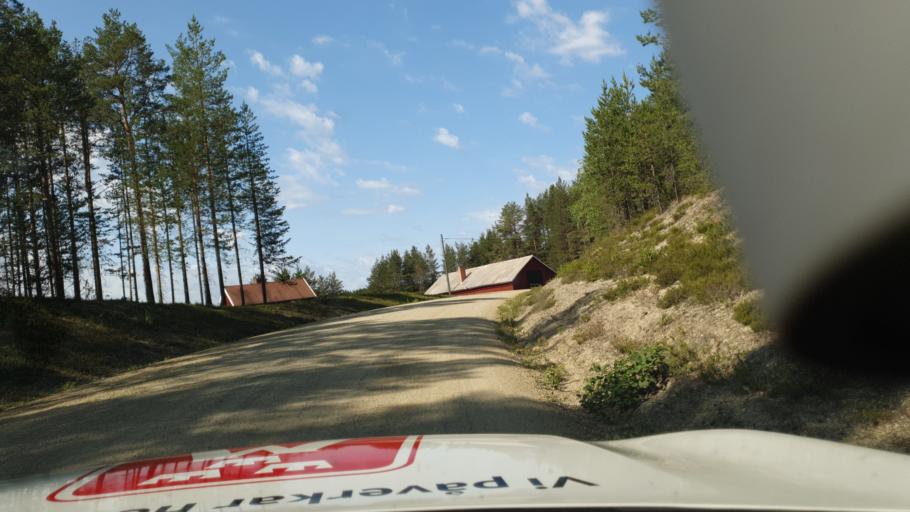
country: SE
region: Vaesterbotten
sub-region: Norsjo Kommun
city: Norsjoe
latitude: 64.6660
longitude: 19.3252
